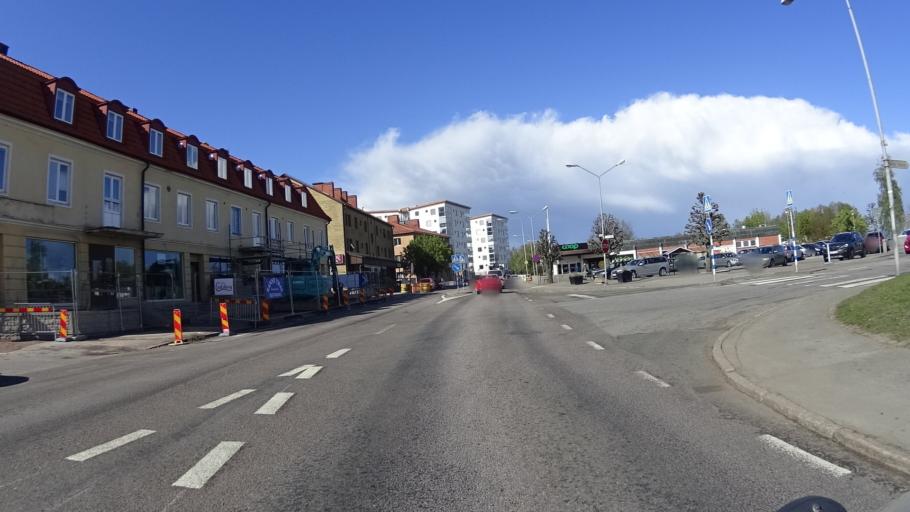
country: SE
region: Vaestra Goetaland
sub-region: Karlsborgs Kommun
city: Karlsborg
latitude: 58.5370
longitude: 14.5046
